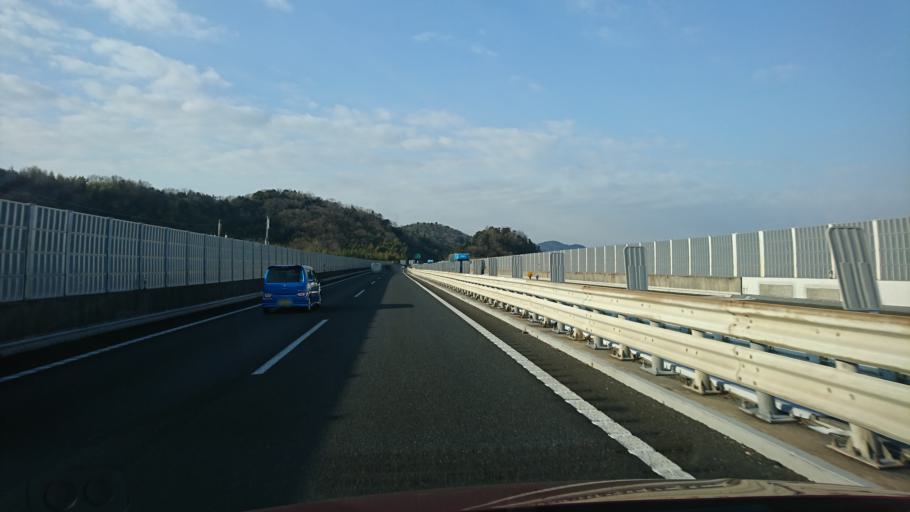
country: JP
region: Hyogo
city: Tatsunocho-tominaga
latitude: 34.8500
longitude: 134.5320
